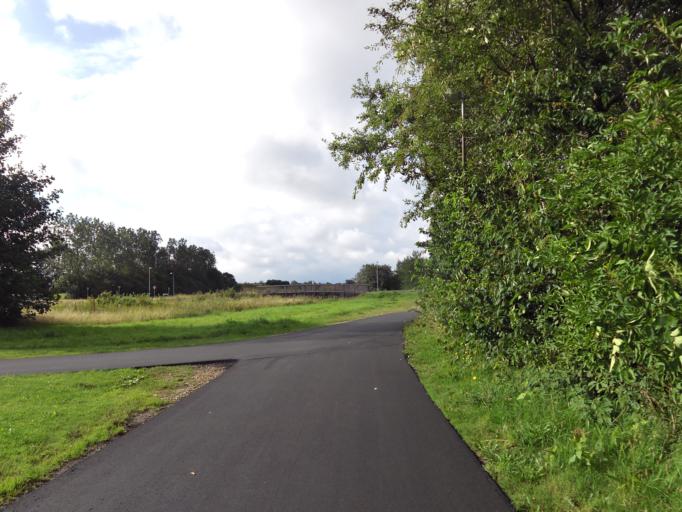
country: DK
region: South Denmark
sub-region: Esbjerg Kommune
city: Ribe
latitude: 55.3367
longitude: 8.7810
